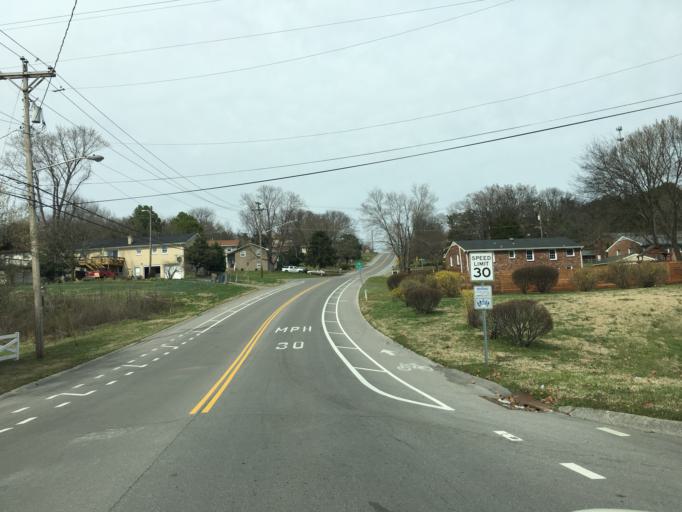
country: US
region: Tennessee
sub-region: Williamson County
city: Brentwood Estates
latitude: 36.0457
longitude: -86.7252
